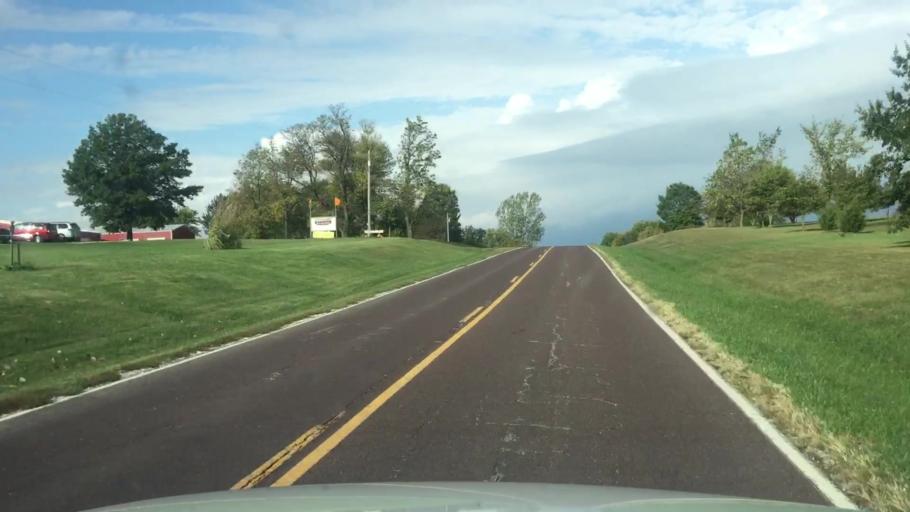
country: US
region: Missouri
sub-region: Boone County
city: Columbia
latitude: 38.8691
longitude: -92.2829
